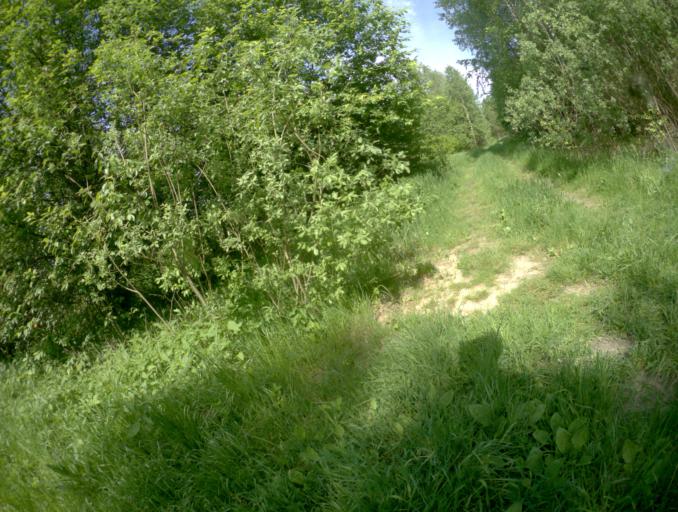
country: RU
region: Vladimir
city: Ivanishchi
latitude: 55.6928
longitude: 40.3740
